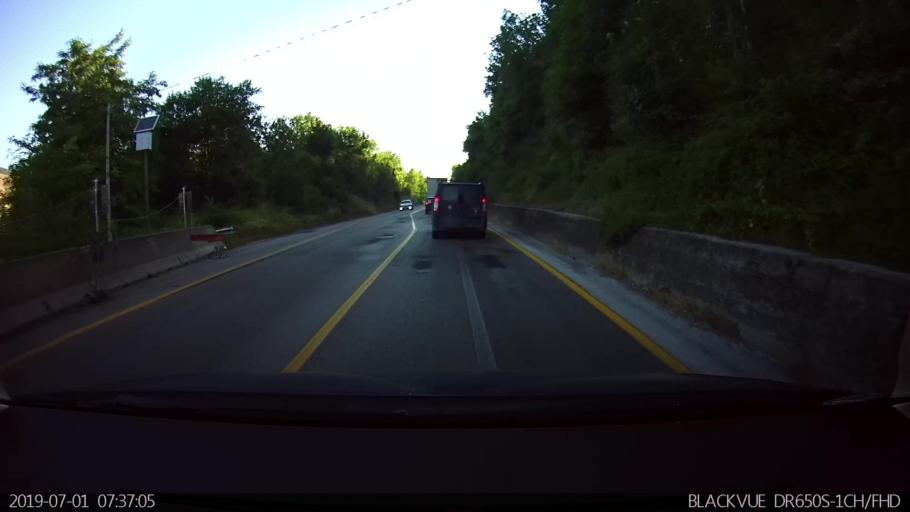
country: IT
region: Latium
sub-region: Provincia di Frosinone
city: Giuliano di Roma
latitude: 41.5354
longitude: 13.2666
